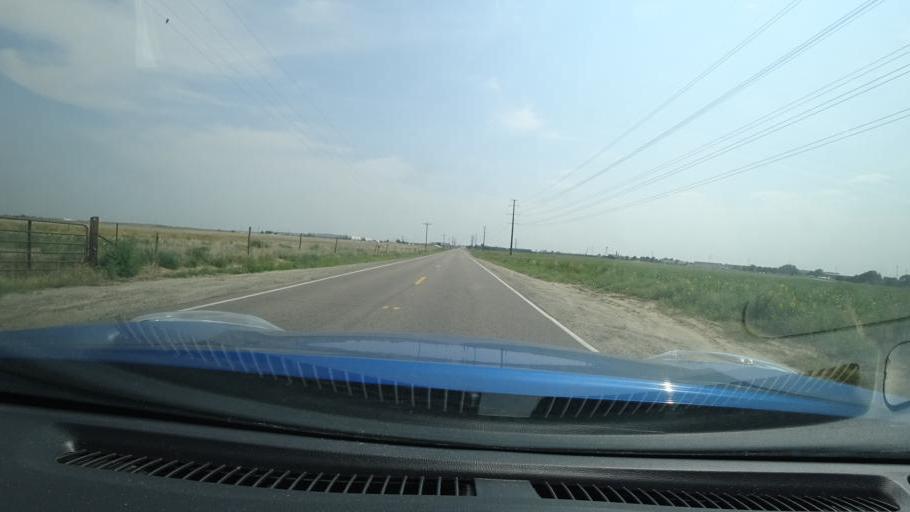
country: US
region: Colorado
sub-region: Adams County
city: Aurora
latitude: 39.7634
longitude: -104.7346
